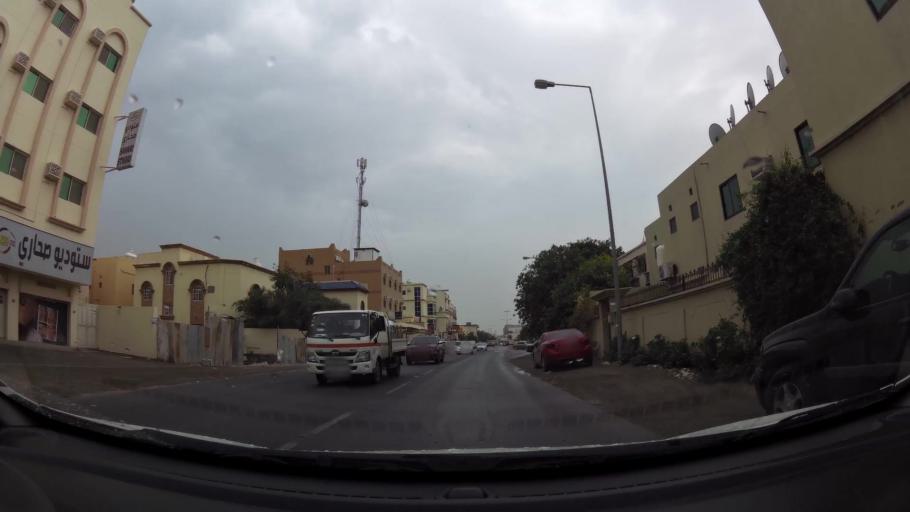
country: BH
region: Northern
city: Madinat `Isa
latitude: 26.1621
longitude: 50.5727
